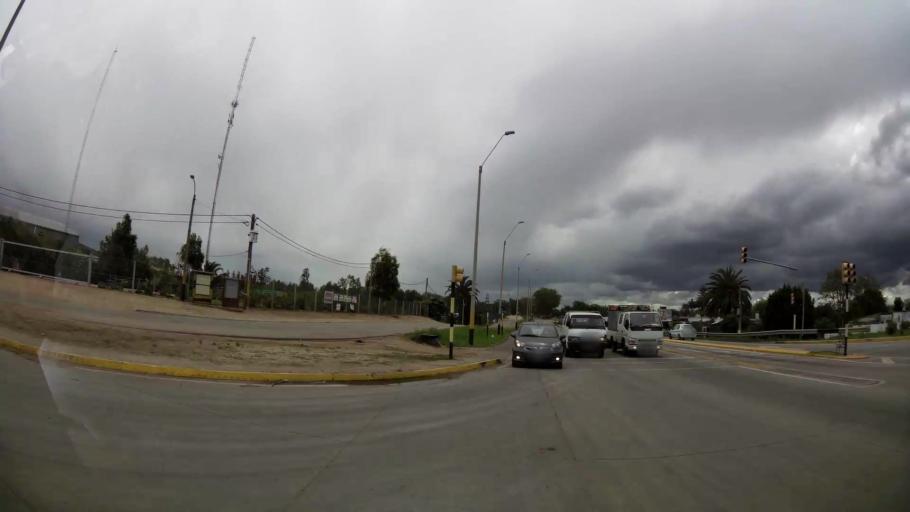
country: UY
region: Canelones
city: Toledo
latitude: -34.7956
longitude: -56.1365
